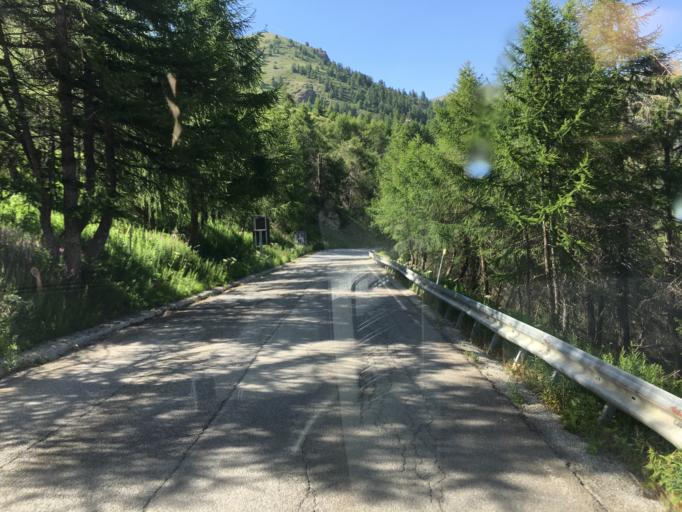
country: IT
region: Piedmont
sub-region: Provincia di Torino
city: Sestriere
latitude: 44.9621
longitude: 6.8836
